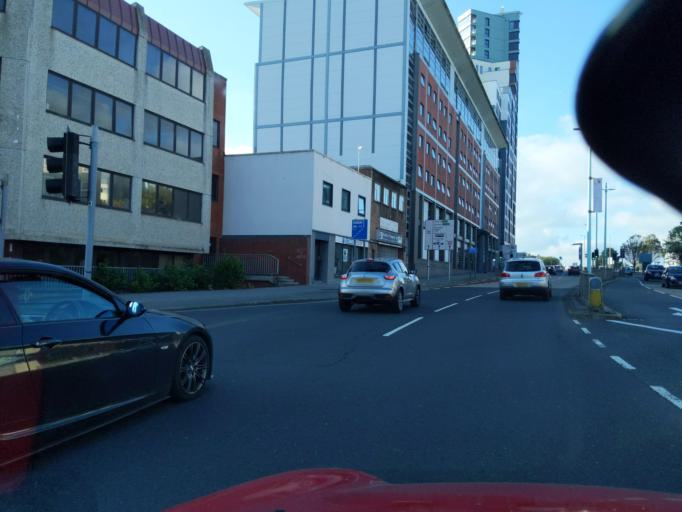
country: GB
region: England
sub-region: Plymouth
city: Plymouth
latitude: 50.3739
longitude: -4.1403
